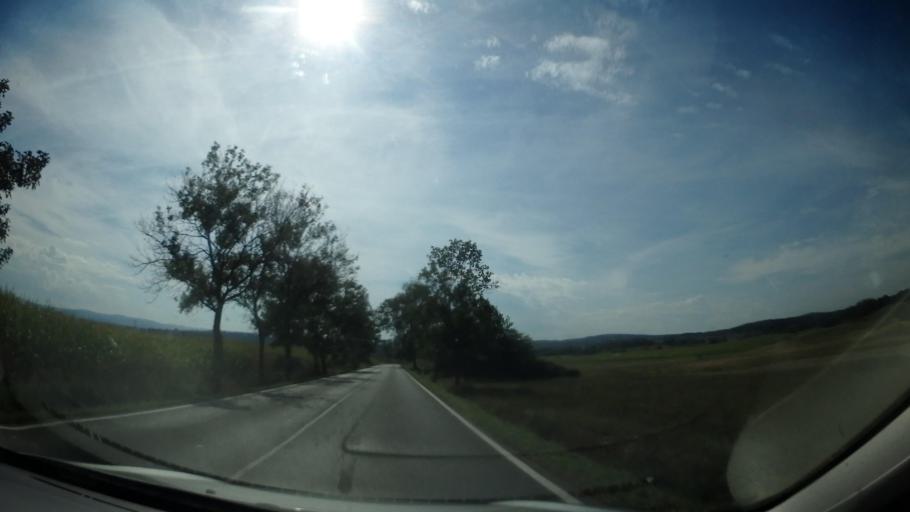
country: CZ
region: Jihocesky
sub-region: Okres Pisek
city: Pisek
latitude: 49.3013
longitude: 14.0643
